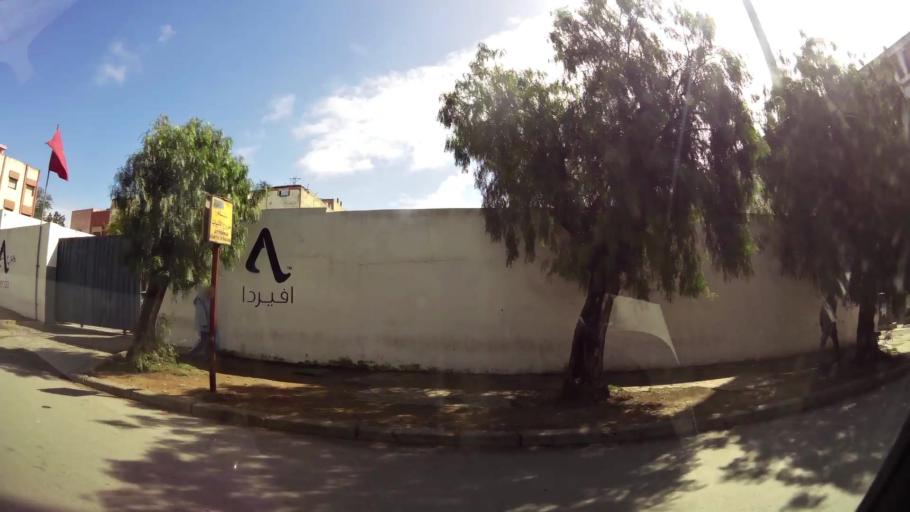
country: MA
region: Grand Casablanca
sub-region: Casablanca
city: Casablanca
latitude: 33.5681
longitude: -7.6773
